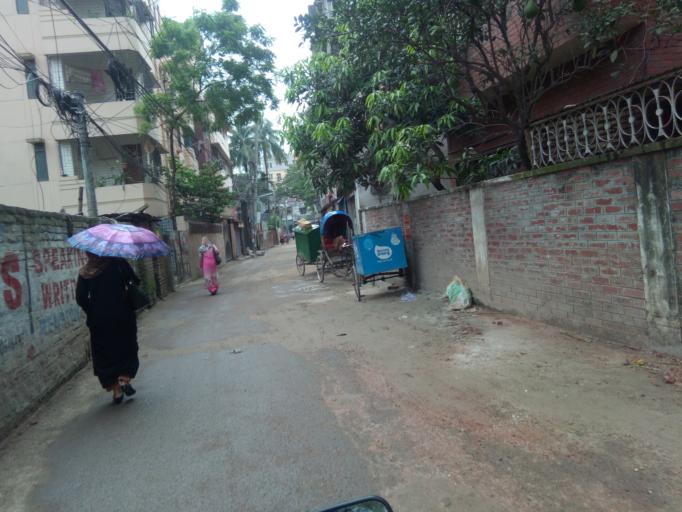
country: BD
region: Dhaka
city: Azimpur
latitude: 23.7570
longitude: 90.3819
